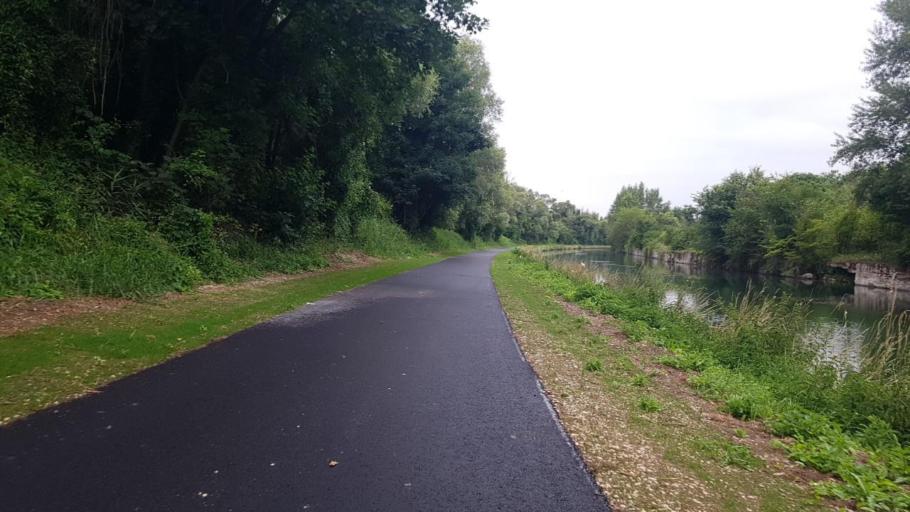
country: FR
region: Champagne-Ardenne
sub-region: Departement de la Marne
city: Vitry-le-Francois
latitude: 48.7759
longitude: 4.5436
